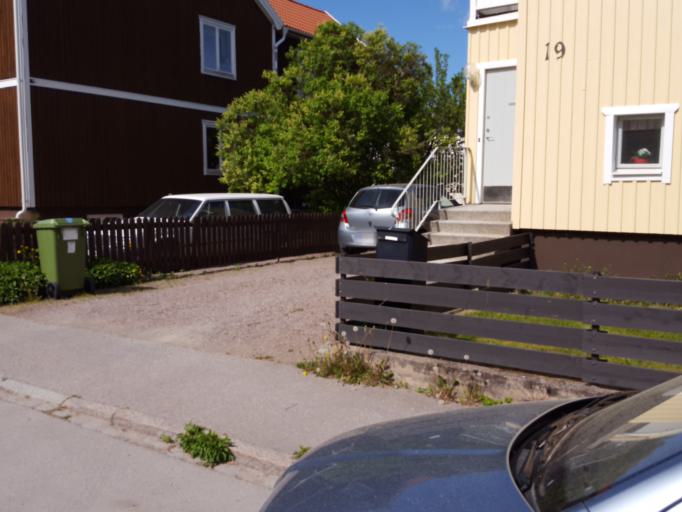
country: SE
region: Uppsala
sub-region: Uppsala Kommun
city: Uppsala
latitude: 59.8600
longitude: 17.6592
